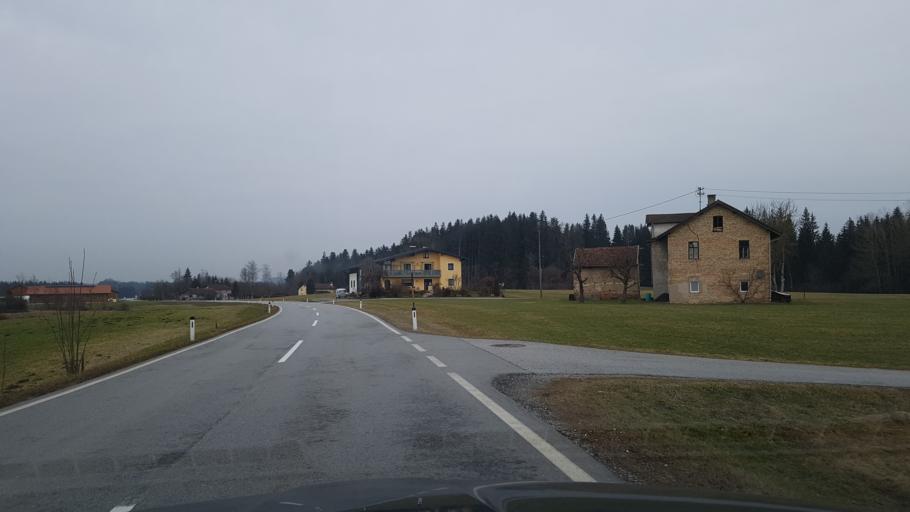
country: AT
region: Salzburg
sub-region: Politischer Bezirk Salzburg-Umgebung
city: Lamprechtshausen
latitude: 48.0354
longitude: 12.9516
